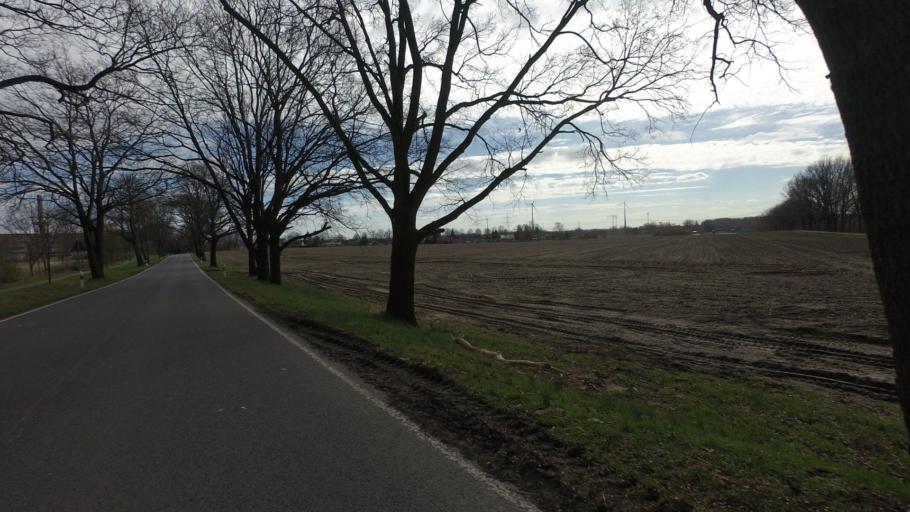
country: DE
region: Berlin
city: Buchholz
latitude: 52.6564
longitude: 13.4299
